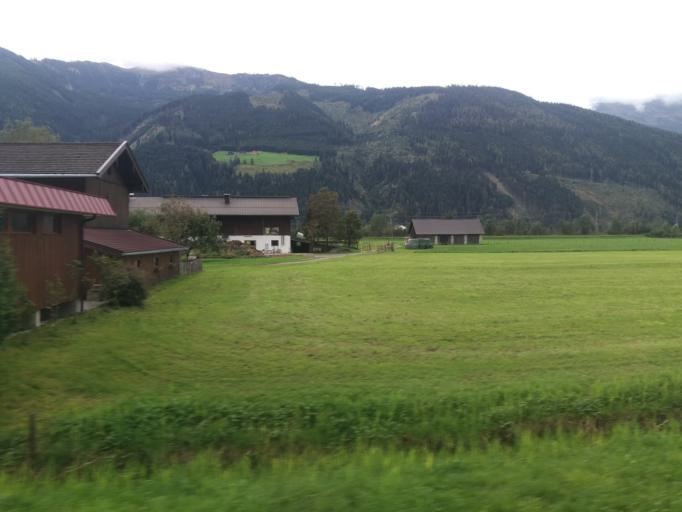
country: AT
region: Salzburg
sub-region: Politischer Bezirk Zell am See
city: Stuhlfelden
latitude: 47.2870
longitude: 12.5204
